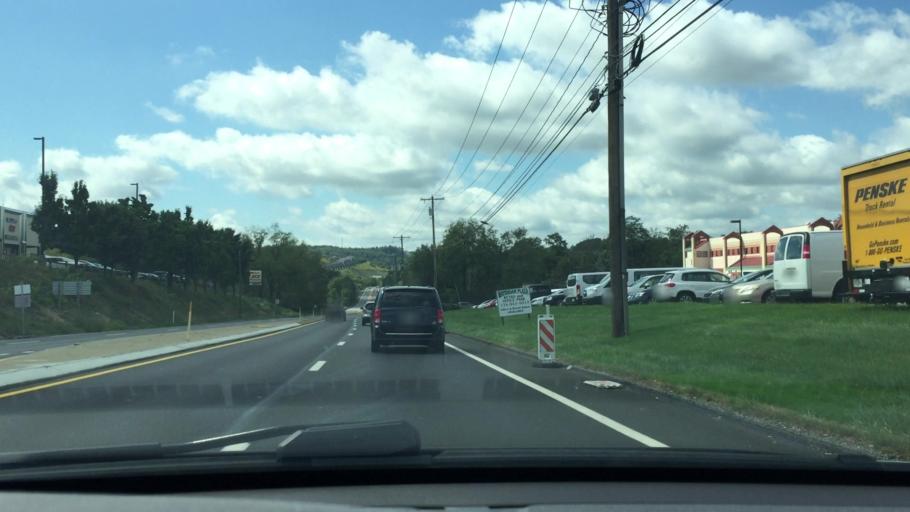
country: US
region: Pennsylvania
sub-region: Washington County
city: Thompsonville
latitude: 40.2624
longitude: -80.1346
